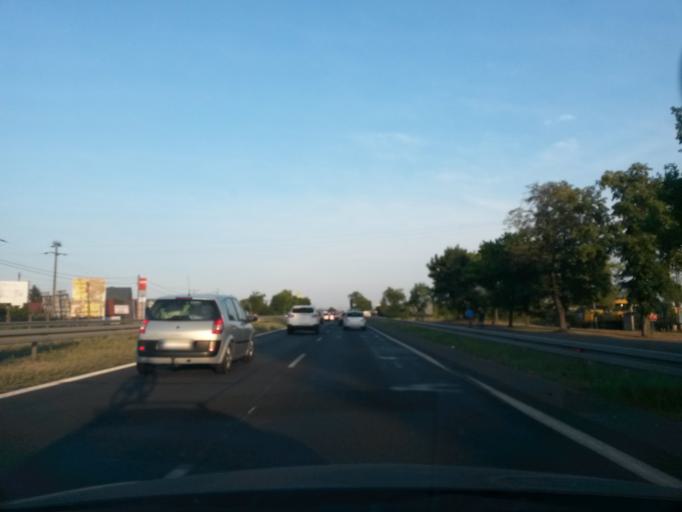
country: PL
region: Masovian Voivodeship
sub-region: Powiat warszawski zachodni
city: Dziekanow Lesny
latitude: 52.3611
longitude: 20.8239
